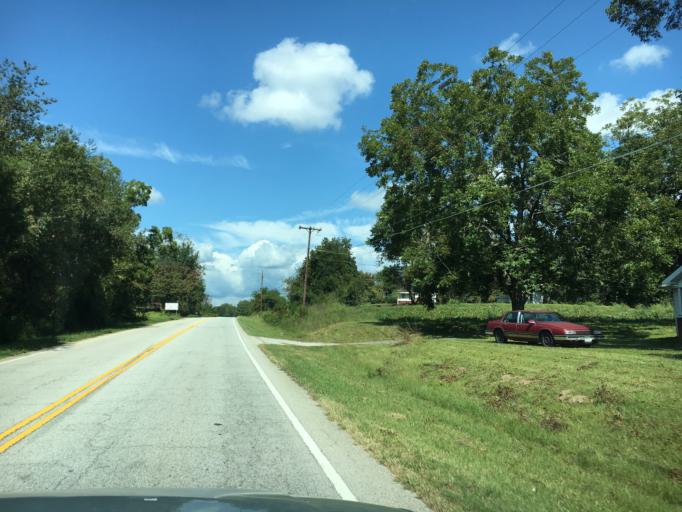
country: US
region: South Carolina
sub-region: Greenville County
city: Tigerville
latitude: 35.0010
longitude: -82.3566
